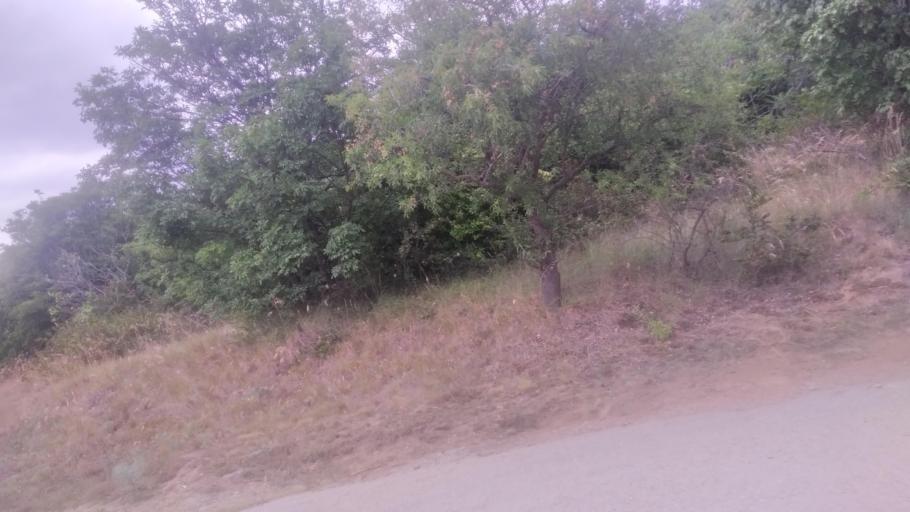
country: HU
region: Veszprem
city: Csopak
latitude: 46.9951
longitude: 17.9671
